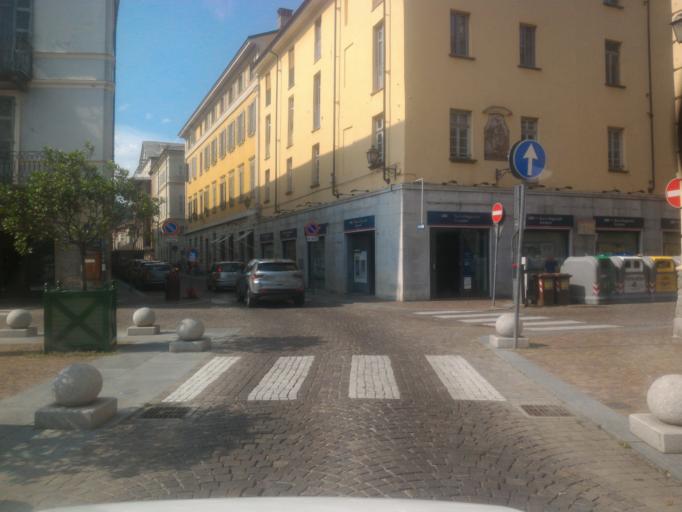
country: IT
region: Piedmont
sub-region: Provincia di Torino
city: Pinerolo
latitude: 44.8855
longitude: 7.3323
